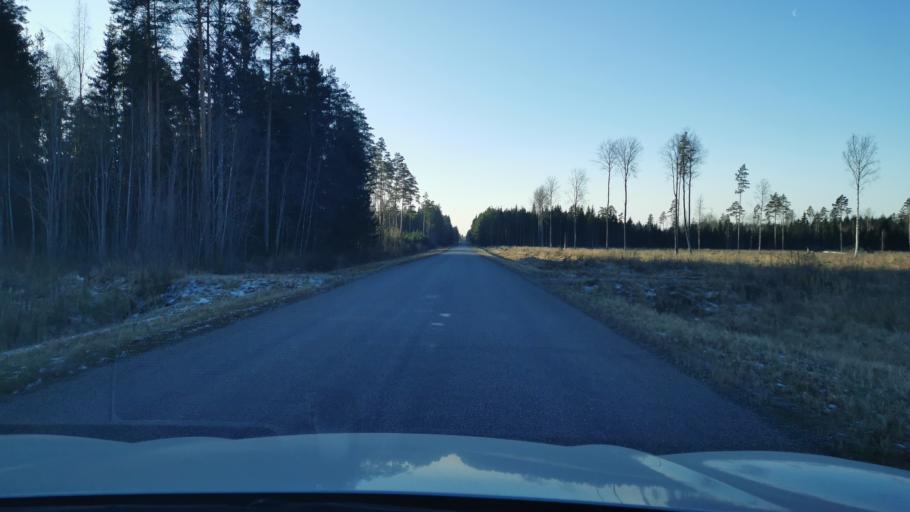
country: EE
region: Ida-Virumaa
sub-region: Kivioli linn
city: Kivioli
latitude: 59.2260
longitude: 26.9612
